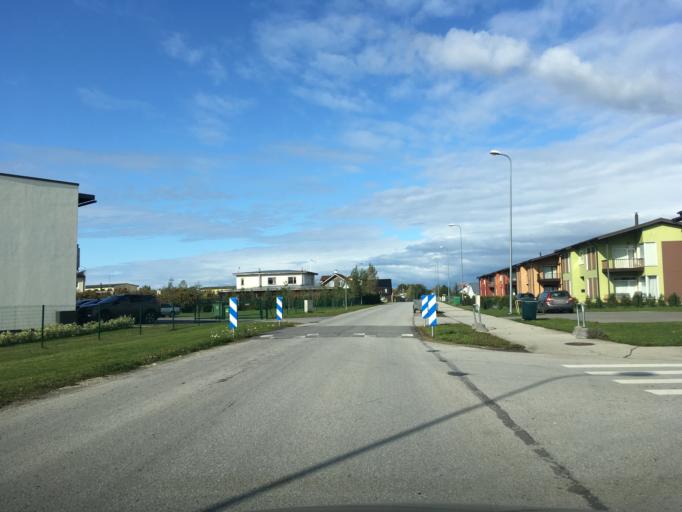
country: EE
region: Harju
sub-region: Saue vald
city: Laagri
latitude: 59.3459
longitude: 24.6428
